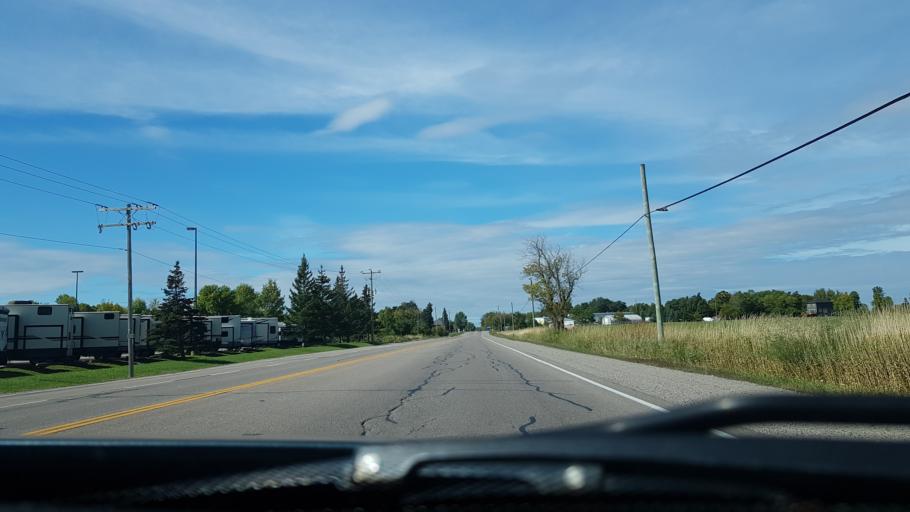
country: CA
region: Ontario
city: Orillia
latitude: 44.5996
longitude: -79.3373
